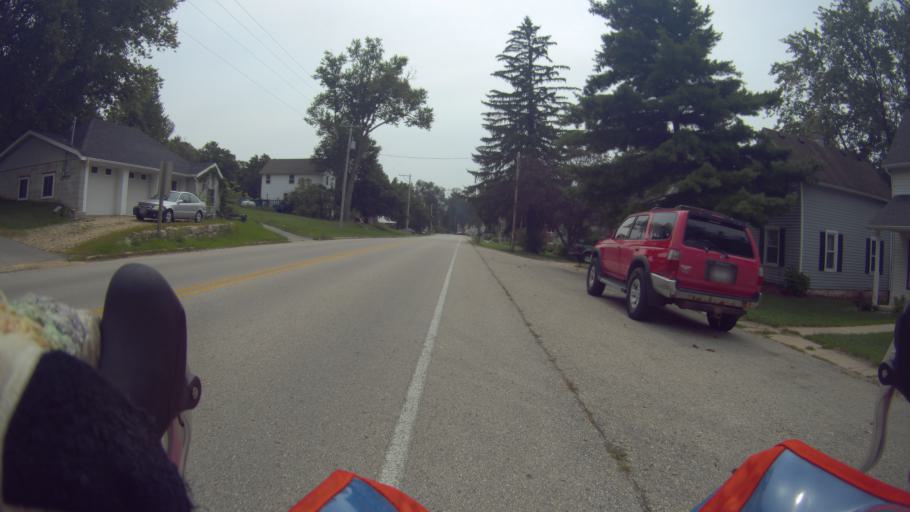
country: US
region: Wisconsin
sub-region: Dane County
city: Mount Horeb
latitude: 42.9481
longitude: -89.6572
